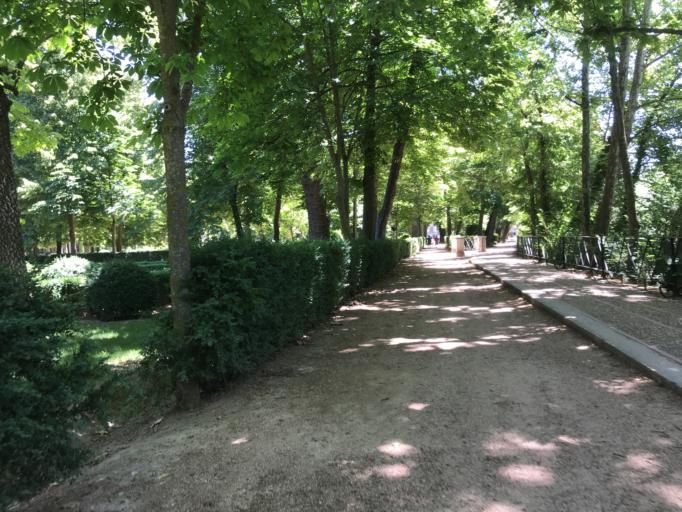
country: ES
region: Madrid
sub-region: Provincia de Madrid
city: Aranjuez
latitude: 40.0384
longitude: -3.6108
